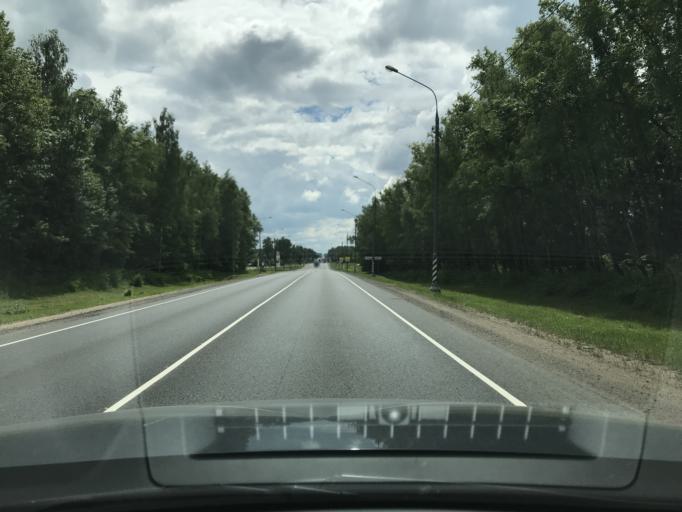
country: RU
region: Moskovskaya
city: Dorokhovo
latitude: 55.3787
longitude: 36.4034
